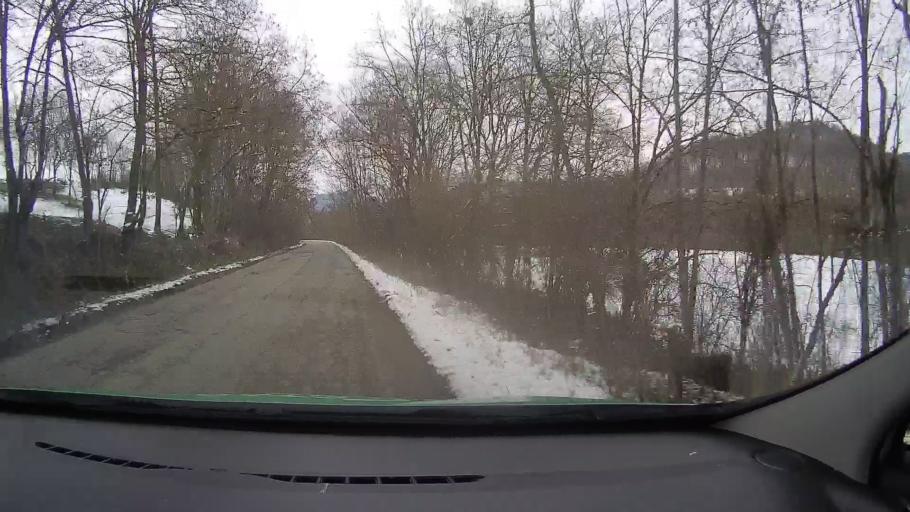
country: RO
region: Hunedoara
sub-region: Comuna Balsa
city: Balsa
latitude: 46.0362
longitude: 23.0789
